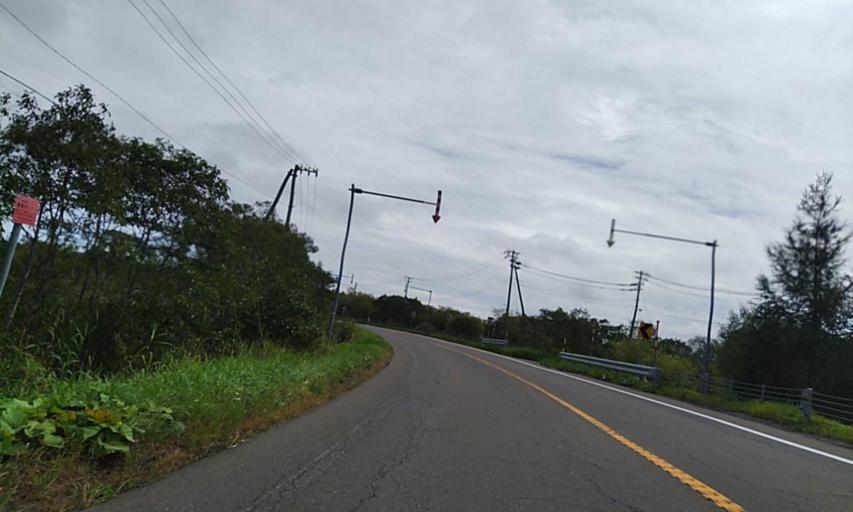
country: JP
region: Hokkaido
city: Shibetsu
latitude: 43.6114
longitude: 145.1829
